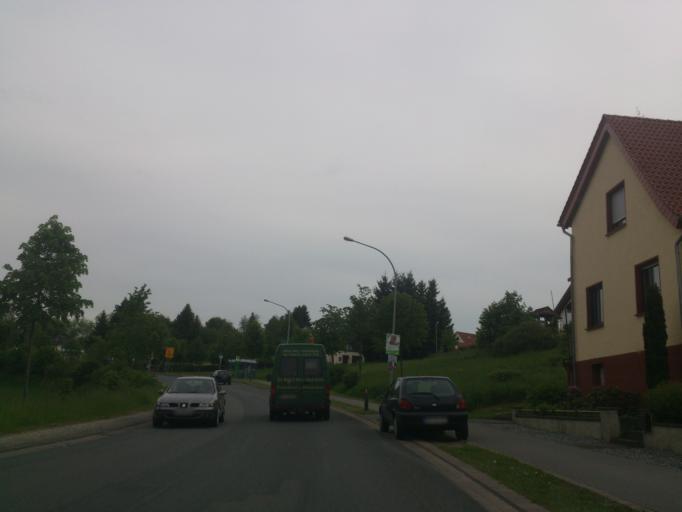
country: DE
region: North Rhine-Westphalia
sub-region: Regierungsbezirk Detmold
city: Altenbeken
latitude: 51.7541
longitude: 8.9516
